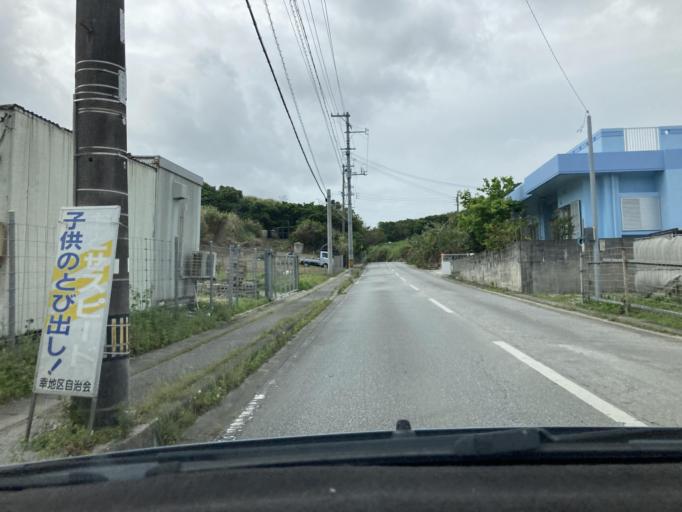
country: JP
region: Okinawa
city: Ginowan
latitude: 26.2310
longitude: 127.7438
